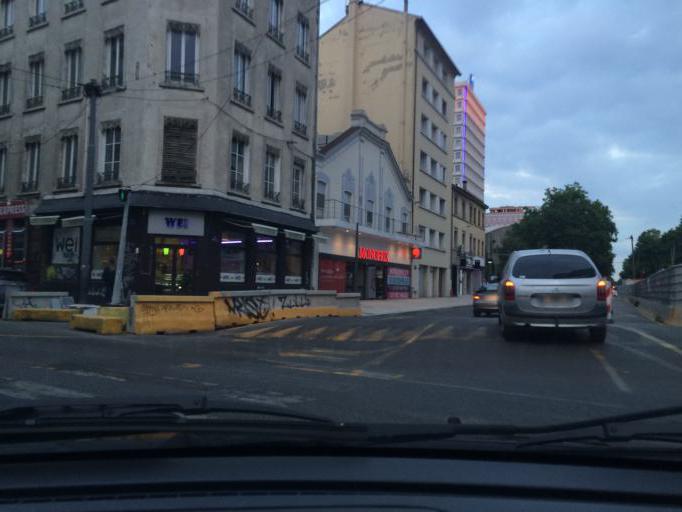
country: FR
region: Rhone-Alpes
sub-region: Departement du Rhone
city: Lyon
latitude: 45.7637
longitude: 4.8515
